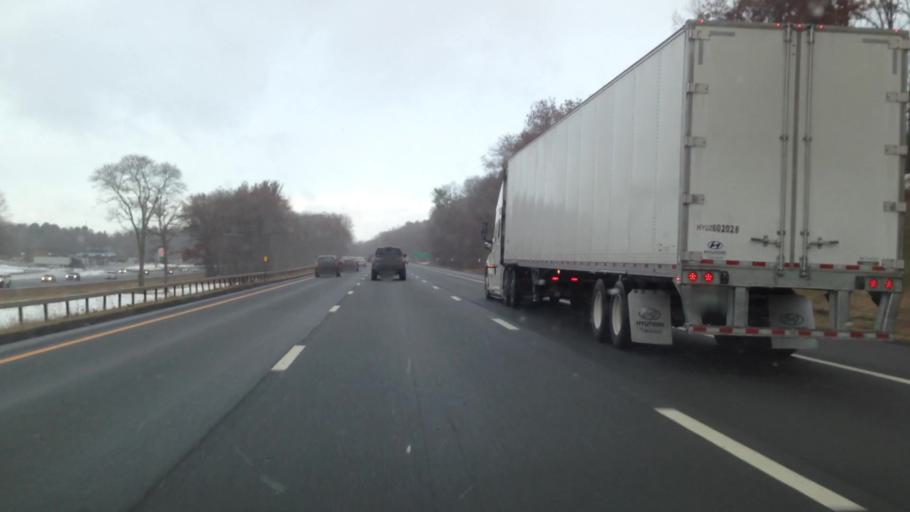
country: US
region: New York
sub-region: Albany County
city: Westmere
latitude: 42.7414
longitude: -73.9123
